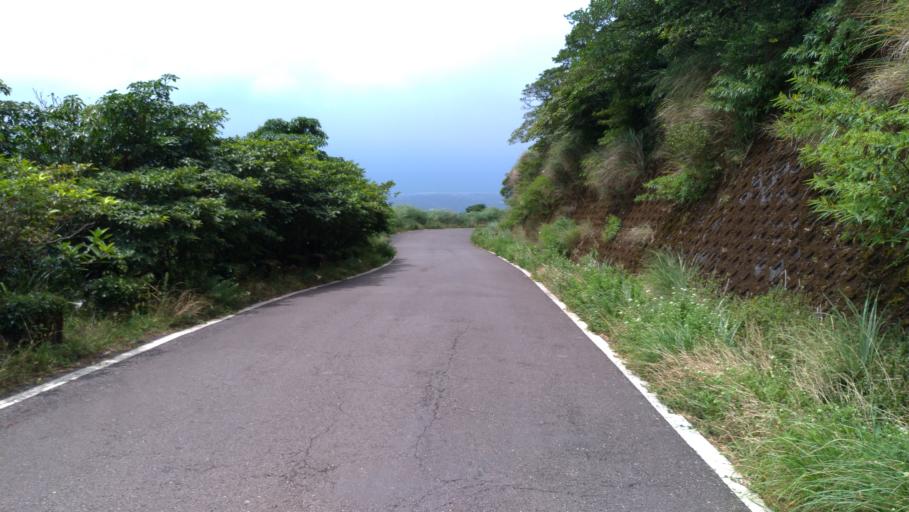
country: TW
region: Taipei
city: Taipei
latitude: 25.1788
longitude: 121.5209
